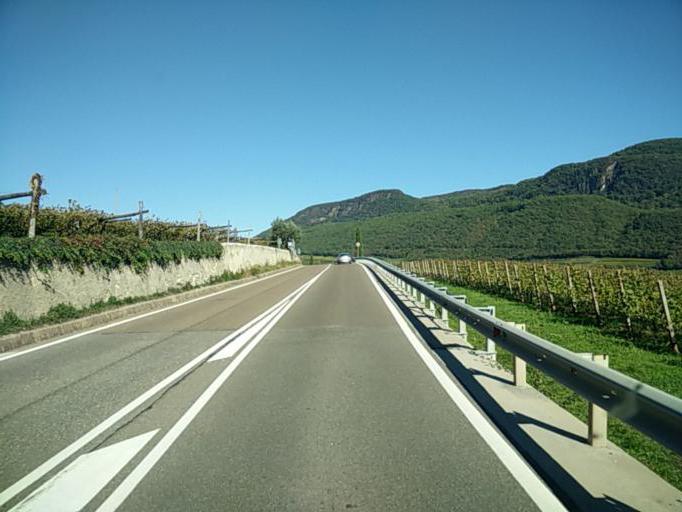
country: IT
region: Trentino-Alto Adige
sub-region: Bolzano
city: Caldaro sulla Strada del Vino
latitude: 46.3868
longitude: 11.2554
